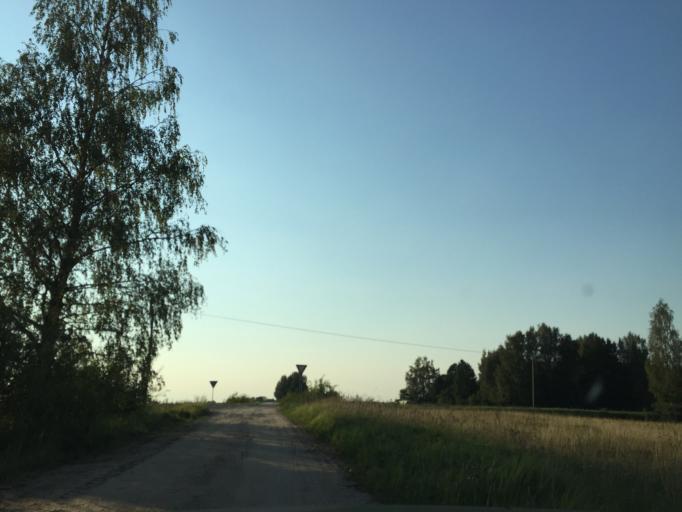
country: LV
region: Limbazu Rajons
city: Limbazi
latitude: 57.5584
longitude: 24.7651
